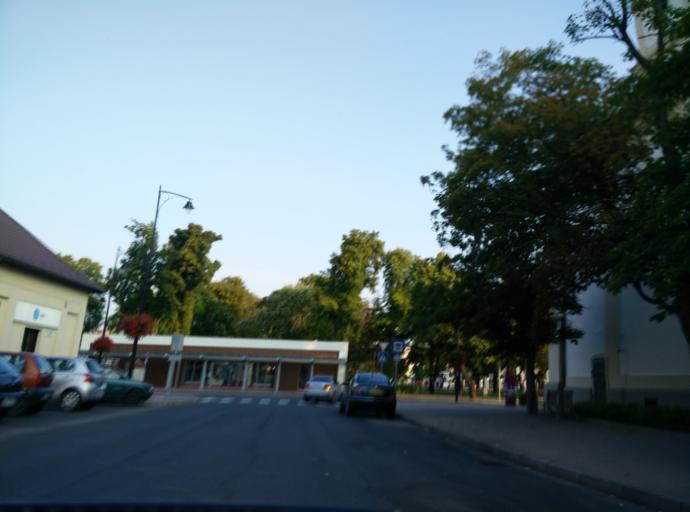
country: HU
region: Heves
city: Hatvan
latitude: 47.6663
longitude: 19.6843
